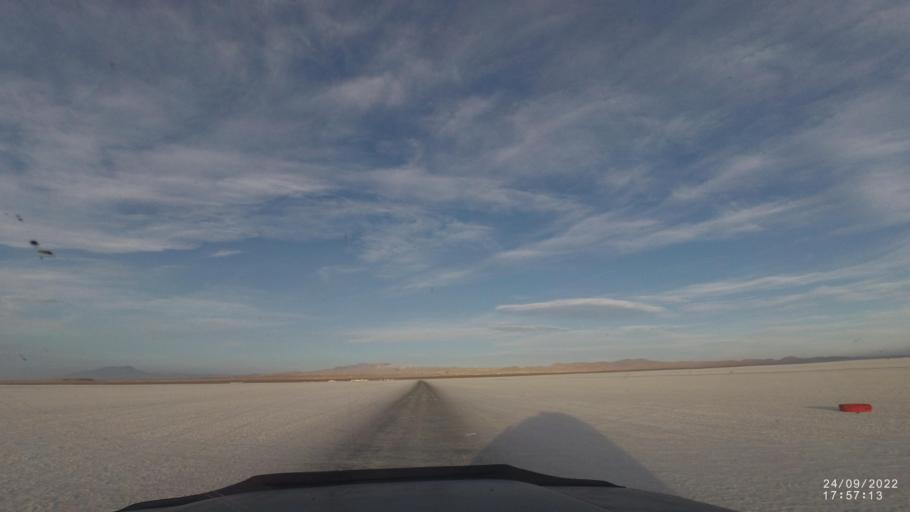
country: BO
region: Potosi
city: Colchani
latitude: -20.3215
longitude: -66.9968
